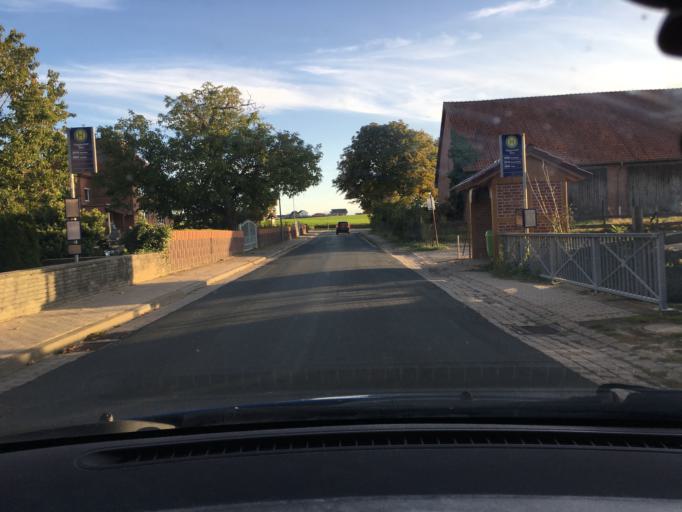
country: DE
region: Lower Saxony
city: Lauenau
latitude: 52.2847
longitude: 9.3810
